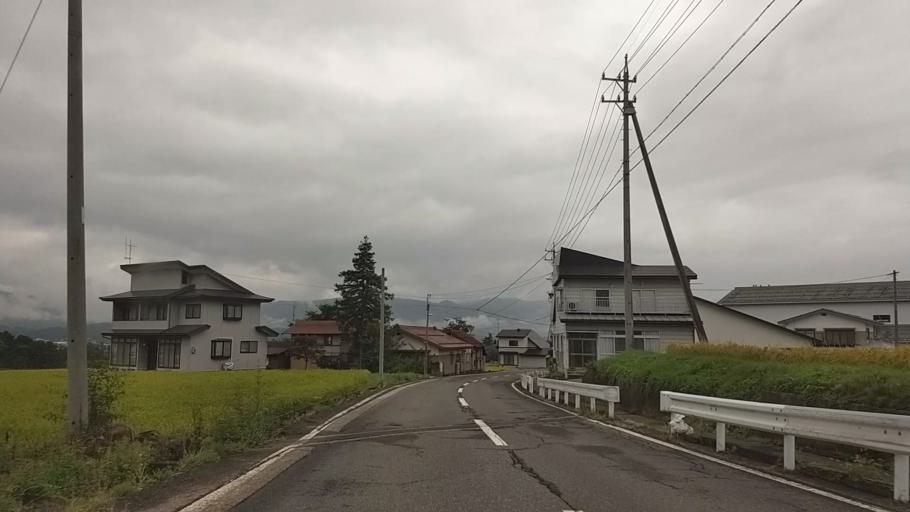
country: JP
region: Nagano
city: Iiyama
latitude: 36.8415
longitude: 138.4064
